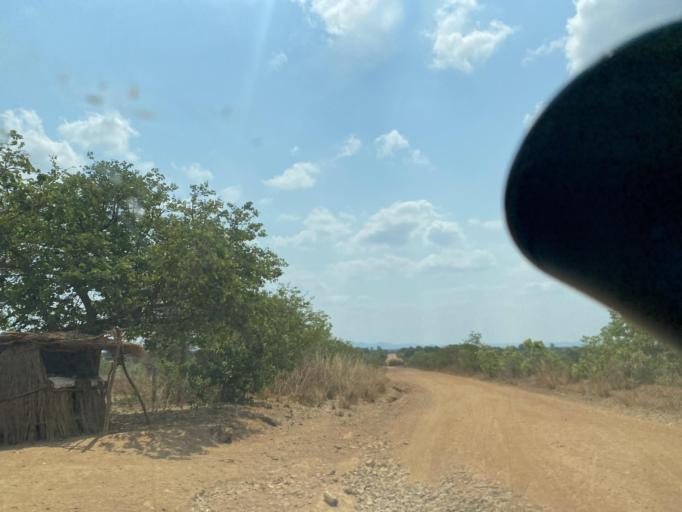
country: ZM
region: Lusaka
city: Chongwe
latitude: -15.5908
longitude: 28.7816
